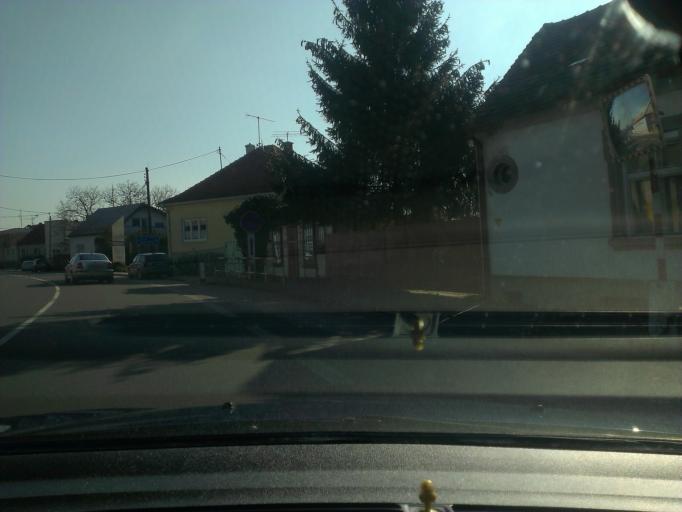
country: SK
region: Trnavsky
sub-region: Okres Trnava
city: Piestany
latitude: 48.6030
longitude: 17.8299
